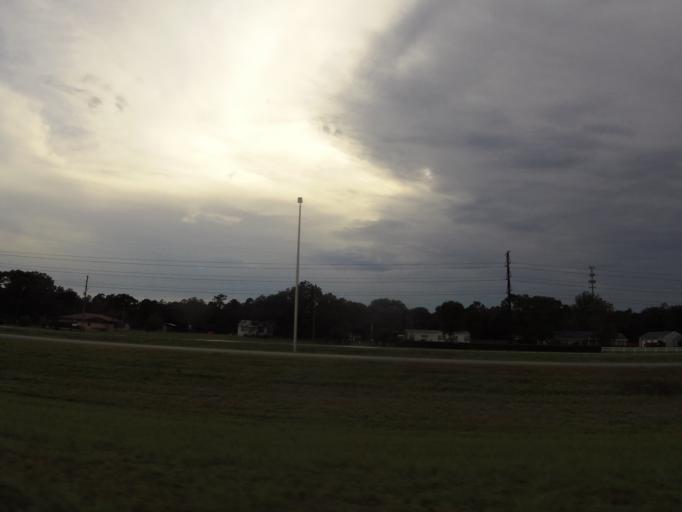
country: US
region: Florida
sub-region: Clay County
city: Lakeside
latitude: 30.1492
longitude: -81.8308
